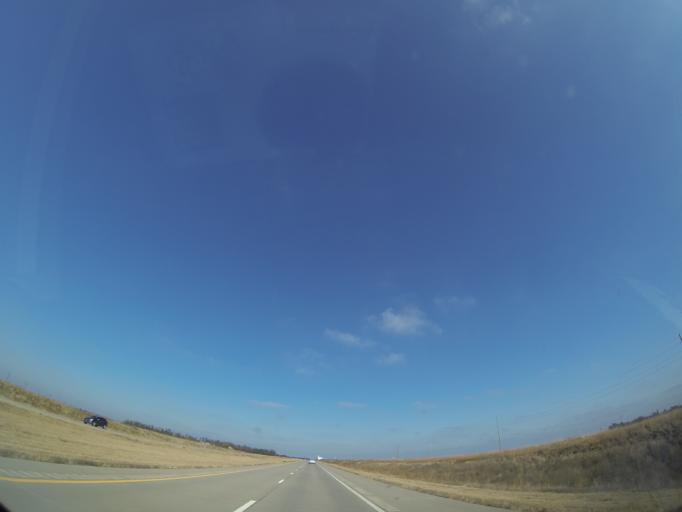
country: US
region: Kansas
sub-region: McPherson County
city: Inman
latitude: 38.2057
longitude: -97.7981
